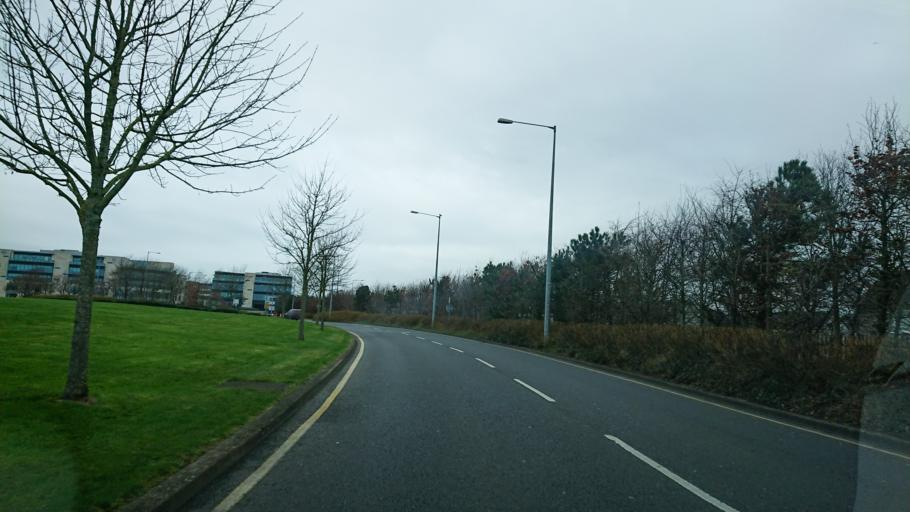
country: IE
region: Munster
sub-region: County Cork
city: Passage West
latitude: 51.8873
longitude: -8.3975
